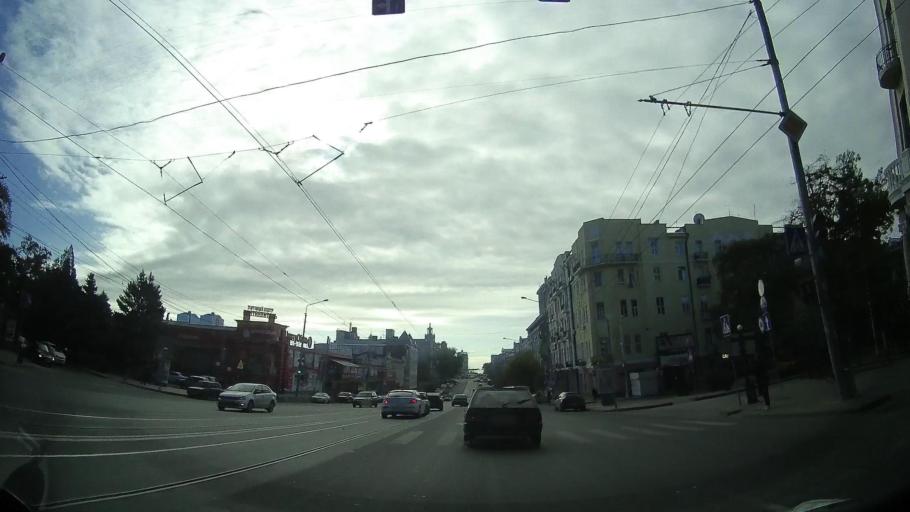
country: RU
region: Rostov
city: Rostov-na-Donu
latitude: 47.2237
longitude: 39.7060
